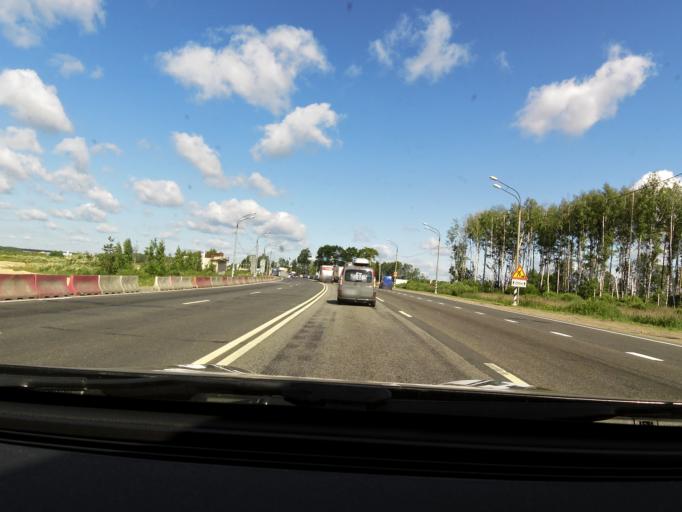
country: RU
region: Tverskaya
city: Tver
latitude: 56.8835
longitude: 35.7802
